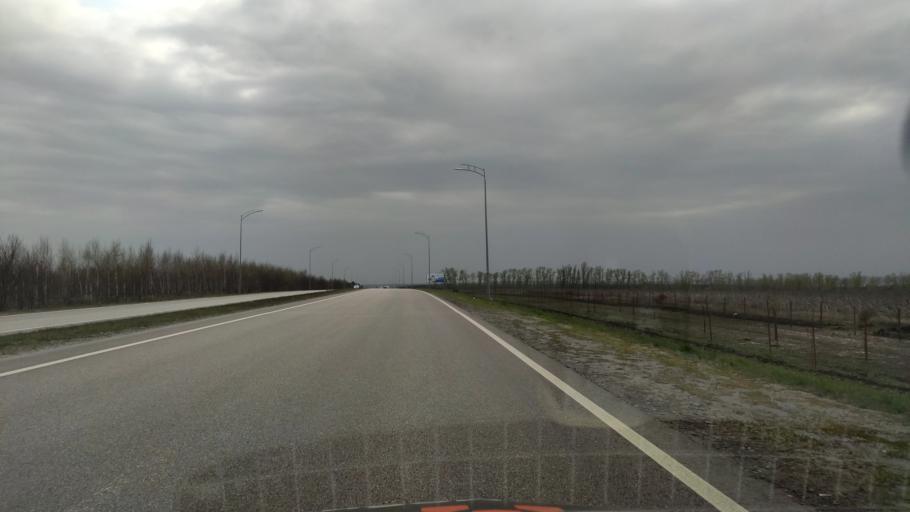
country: RU
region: Belgorod
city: Staryy Oskol
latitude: 51.3800
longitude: 37.8535
